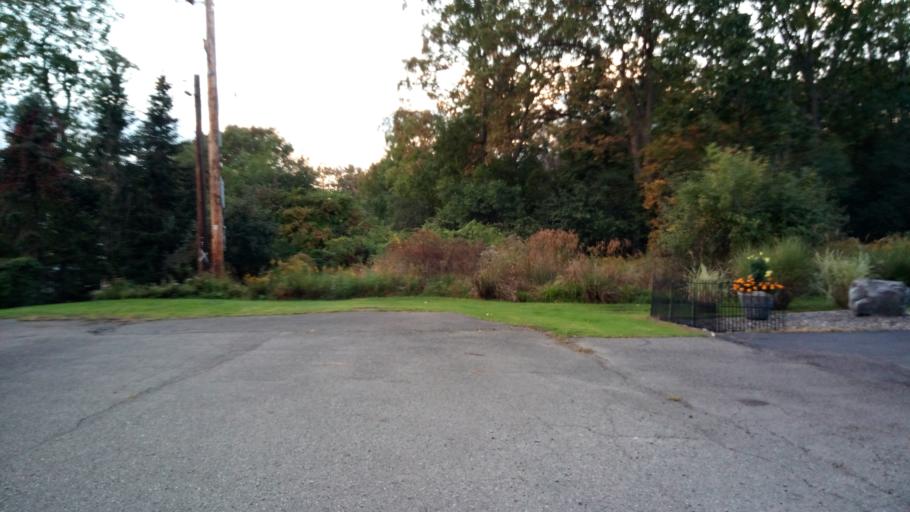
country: US
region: New York
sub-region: Chemung County
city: West Elmira
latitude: 42.0881
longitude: -76.8384
